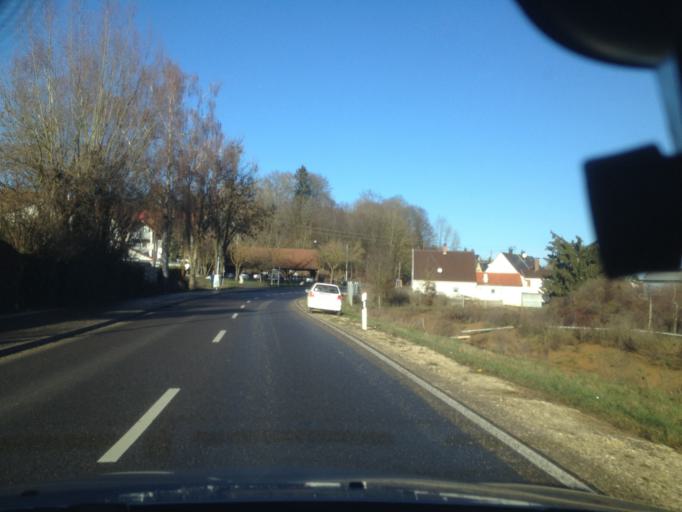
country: DE
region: Bavaria
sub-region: Swabia
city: Offingen
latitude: 48.4755
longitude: 10.3637
